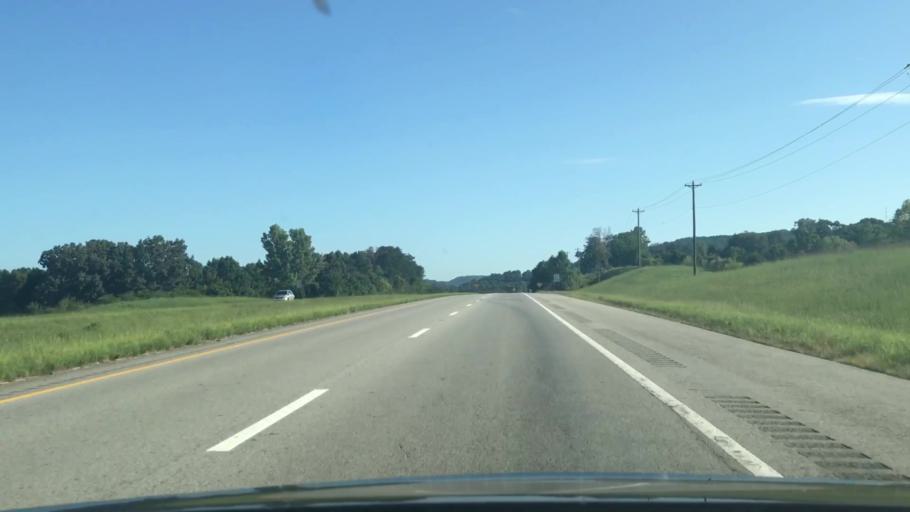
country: US
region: Tennessee
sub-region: Overton County
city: Livingston
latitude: 36.3537
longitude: -85.3437
